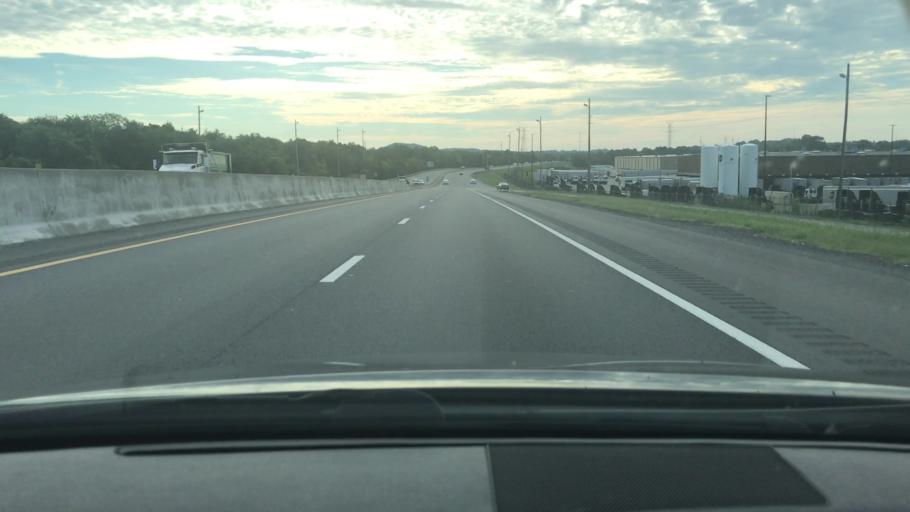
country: US
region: Tennessee
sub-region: Davidson County
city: Nashville
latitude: 36.2340
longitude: -86.8144
